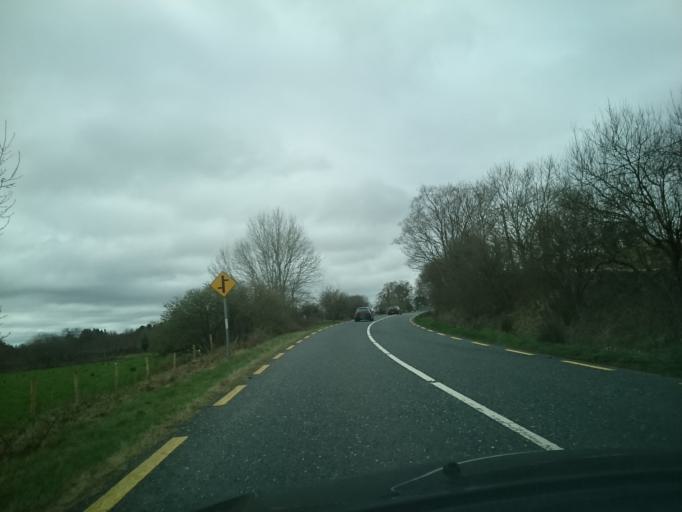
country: IE
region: Connaught
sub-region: Maigh Eo
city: Castlebar
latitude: 53.8199
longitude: -9.3691
